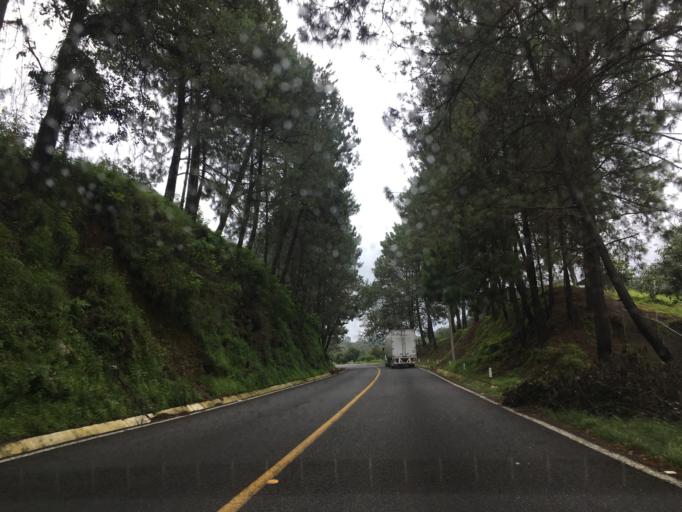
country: MX
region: Michoacan
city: Tingambato
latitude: 19.4751
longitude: -101.9137
